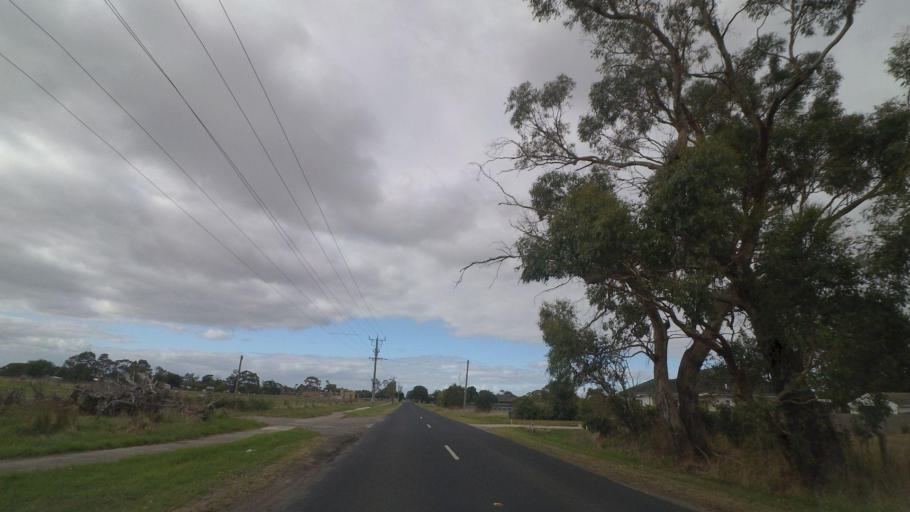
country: AU
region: Victoria
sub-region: Cardinia
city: Pakenham South
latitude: -38.0775
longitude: 145.5711
